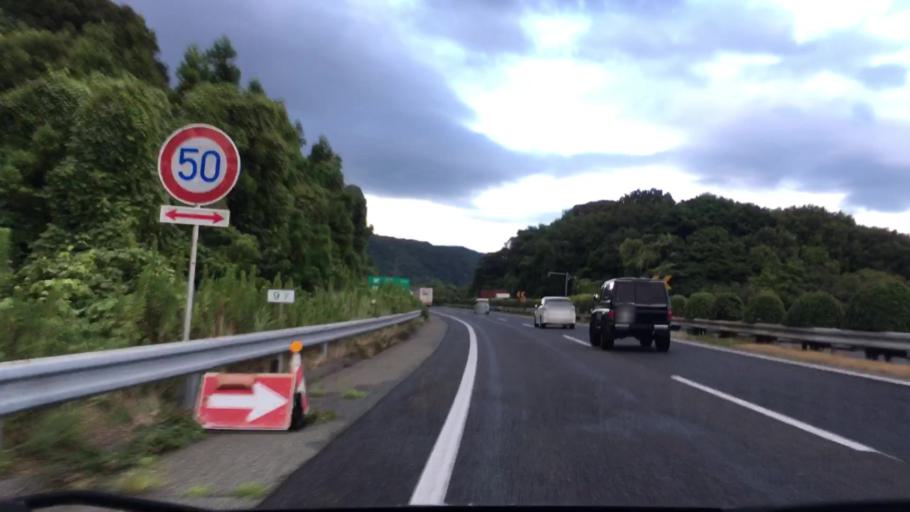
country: JP
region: Fukuoka
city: Kanda
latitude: 33.8544
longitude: 130.9368
